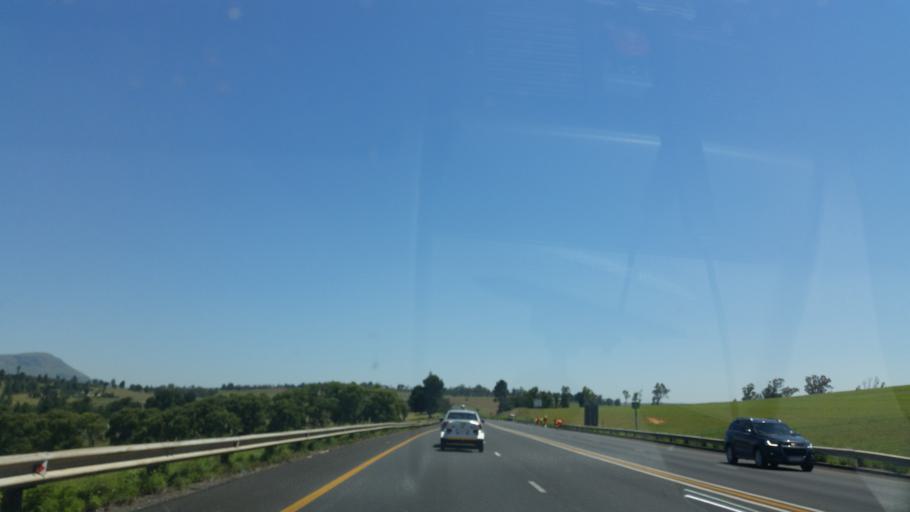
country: ZA
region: Orange Free State
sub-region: Thabo Mofutsanyana District Municipality
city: Harrismith
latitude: -28.3533
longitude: 29.2842
